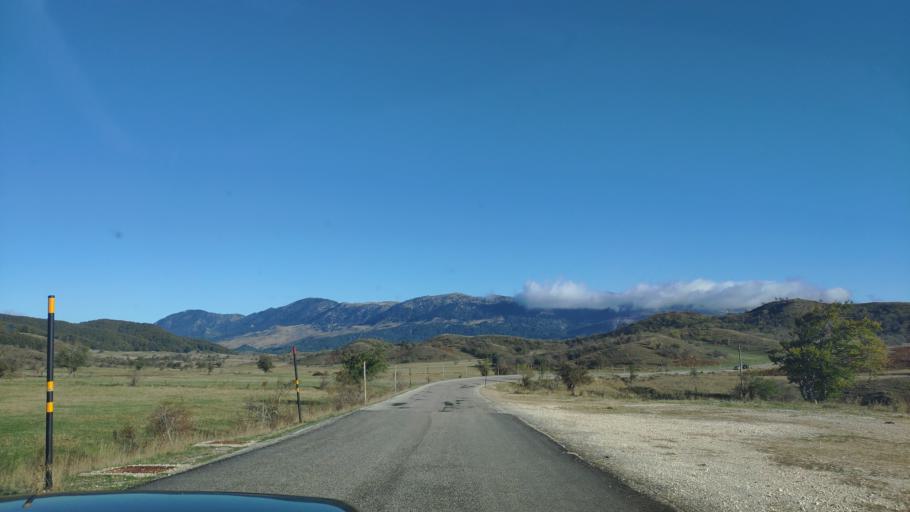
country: GR
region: Epirus
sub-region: Nomos Ioanninon
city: Metsovo
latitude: 39.7858
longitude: 21.1587
